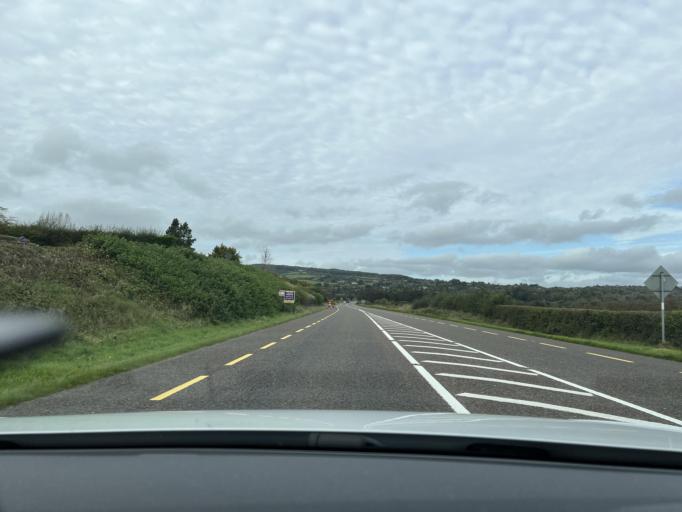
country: IE
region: Connaught
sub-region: Roscommon
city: Boyle
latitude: 53.9815
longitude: -8.2778
